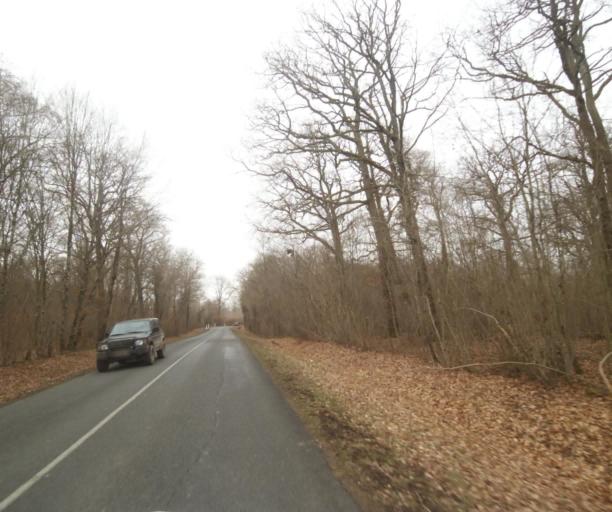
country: FR
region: Champagne-Ardenne
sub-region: Departement de la Marne
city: Pargny-sur-Saulx
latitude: 48.7279
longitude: 4.8680
